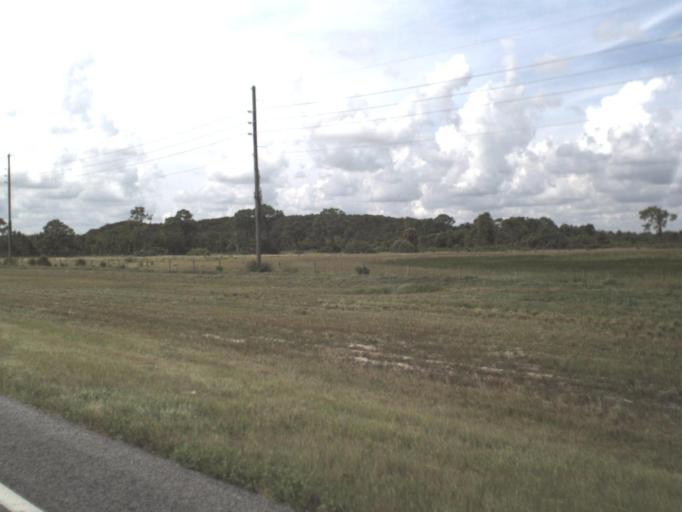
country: US
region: Florida
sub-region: Okeechobee County
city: Taylor Creek
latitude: 27.2968
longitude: -80.6880
